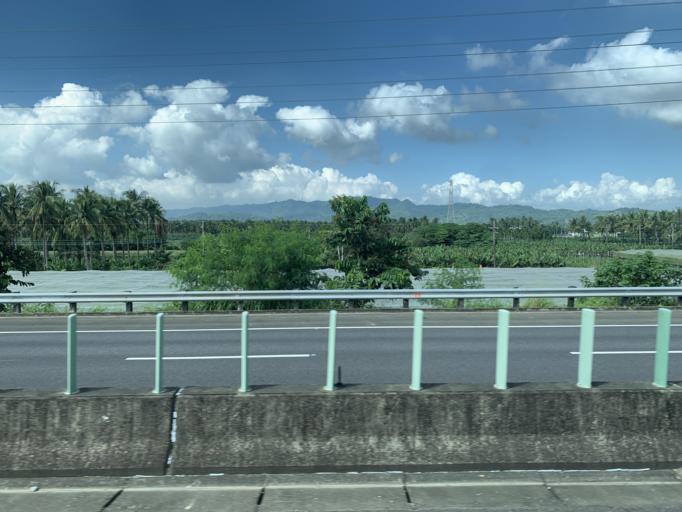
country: TW
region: Taiwan
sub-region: Pingtung
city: Pingtung
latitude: 22.8447
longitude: 120.4959
